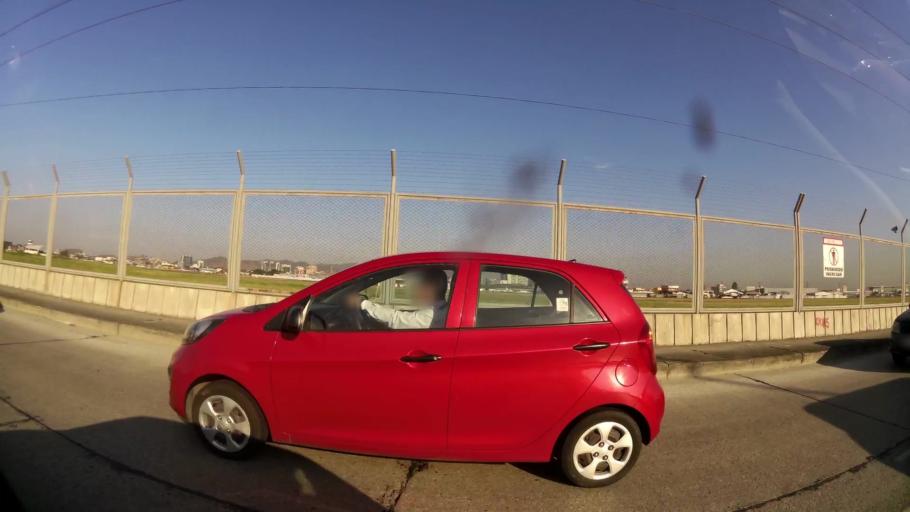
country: EC
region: Guayas
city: Eloy Alfaro
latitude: -2.1575
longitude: -79.8805
